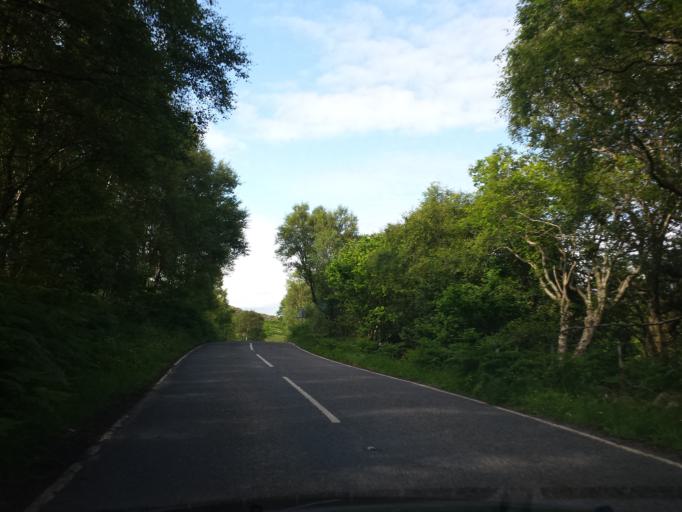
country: GB
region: Scotland
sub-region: Argyll and Bute
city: Isle Of Mull
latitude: 56.9603
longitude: -5.8357
